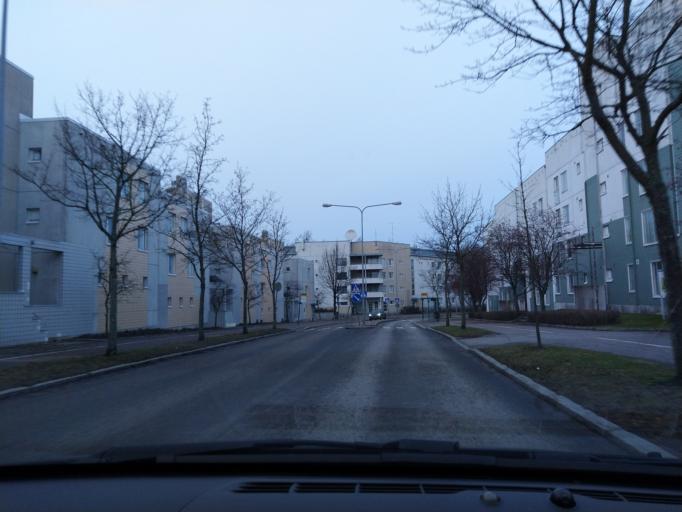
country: FI
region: Uusimaa
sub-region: Helsinki
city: Vantaa
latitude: 60.2383
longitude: 25.0675
